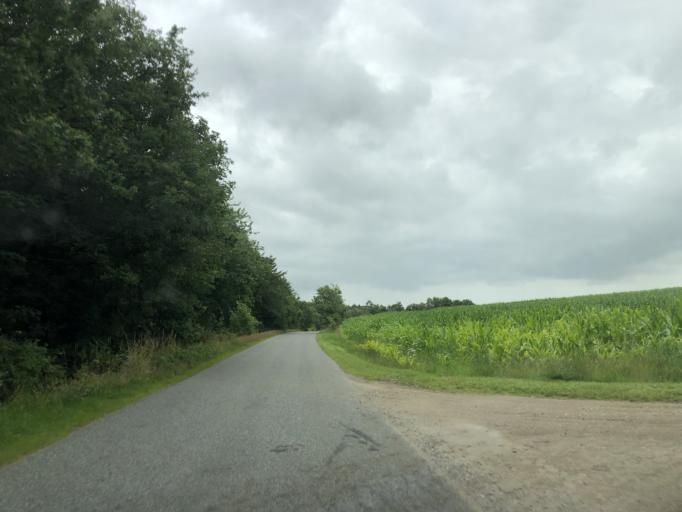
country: DK
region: Central Jutland
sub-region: Herning Kommune
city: Snejbjerg
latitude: 56.1939
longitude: 8.8453
